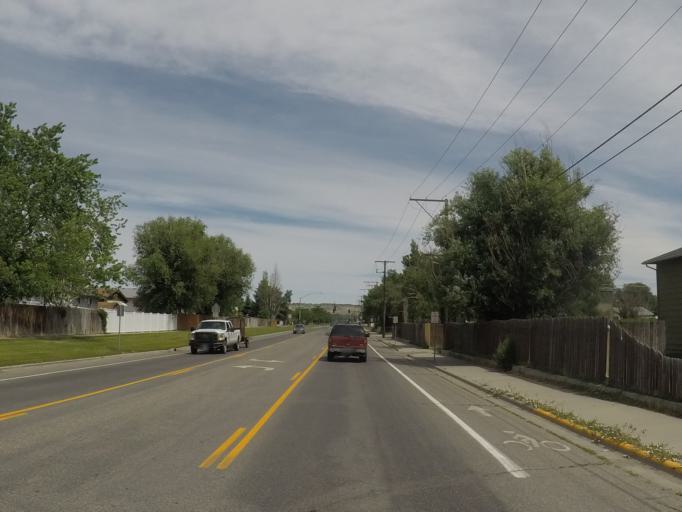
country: US
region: Montana
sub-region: Yellowstone County
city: Billings
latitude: 45.7605
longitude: -108.5968
